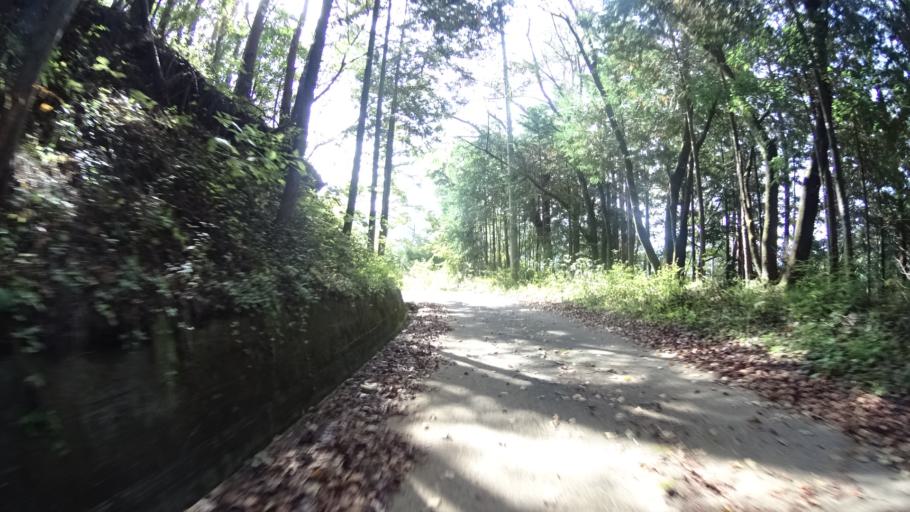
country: JP
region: Yamanashi
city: Otsuki
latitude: 35.5740
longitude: 138.9878
